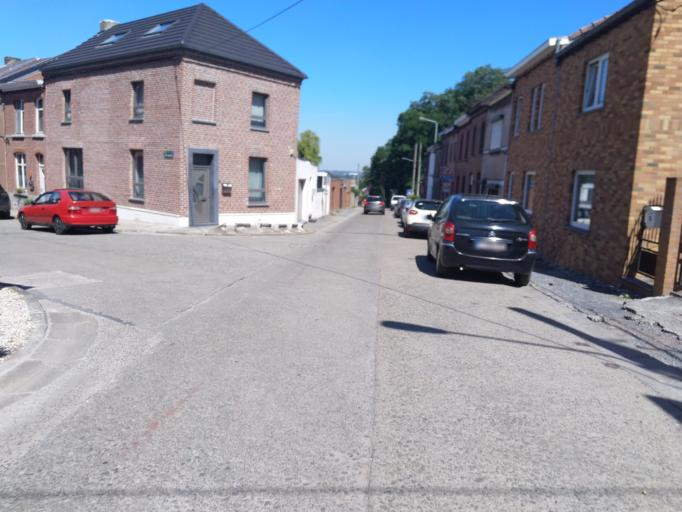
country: BE
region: Wallonia
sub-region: Province du Hainaut
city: Colfontaine
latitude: 50.4233
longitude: 3.8693
